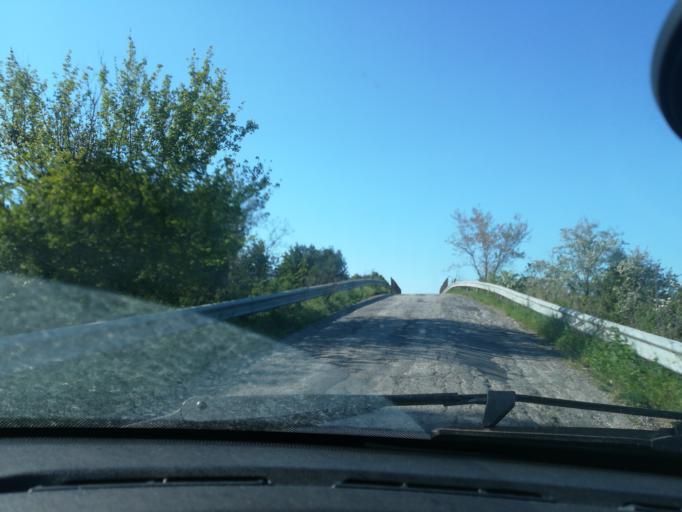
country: IT
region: The Marches
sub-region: Provincia di Macerata
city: Zona Industriale
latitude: 43.2667
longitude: 13.4935
